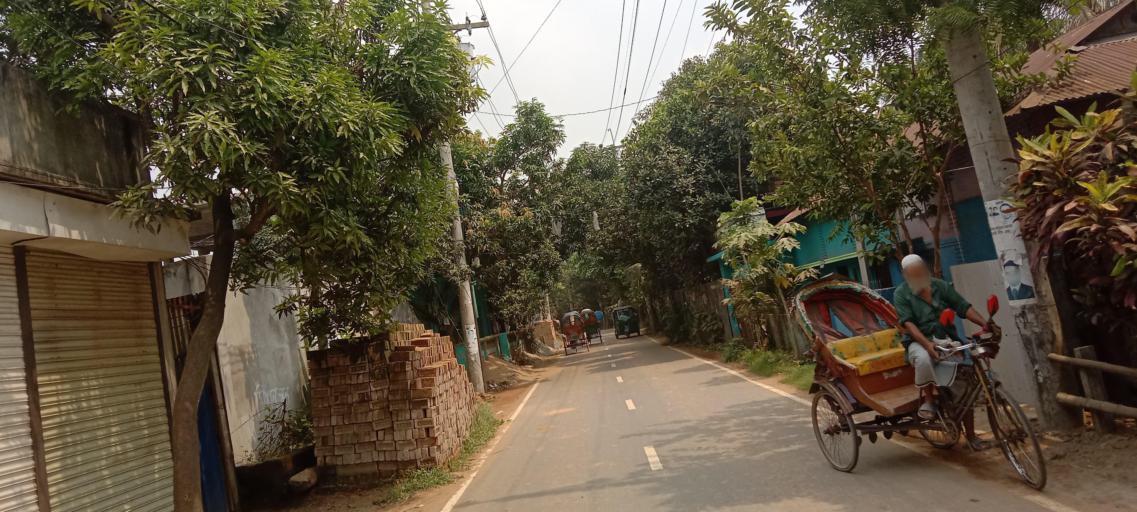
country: BD
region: Dhaka
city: Azimpur
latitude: 23.7253
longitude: 90.2736
